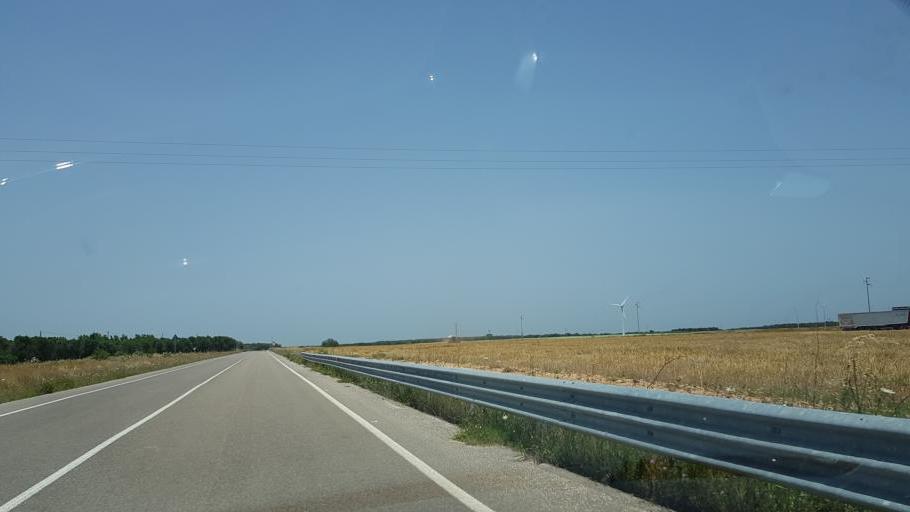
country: IT
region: Apulia
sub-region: Provincia di Brindisi
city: Mesagne
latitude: 40.5011
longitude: 17.8285
